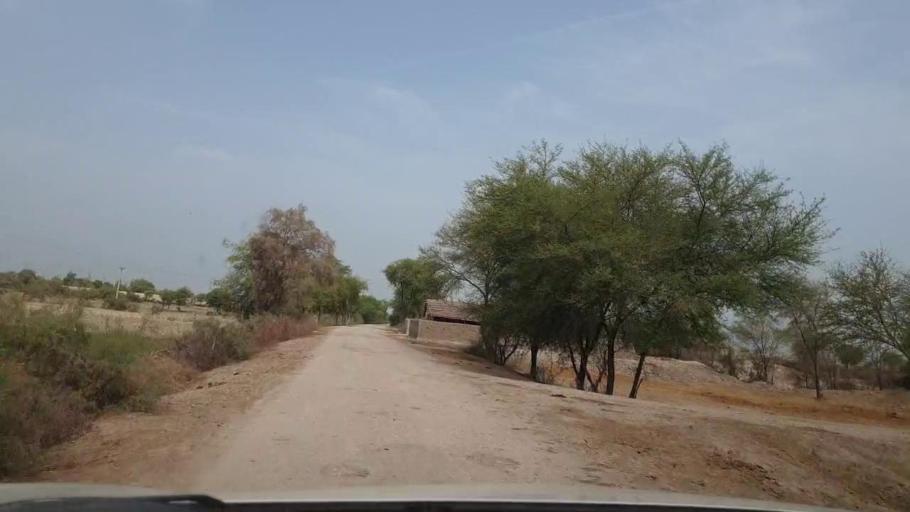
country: PK
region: Sindh
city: Dokri
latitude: 27.4039
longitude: 68.2467
